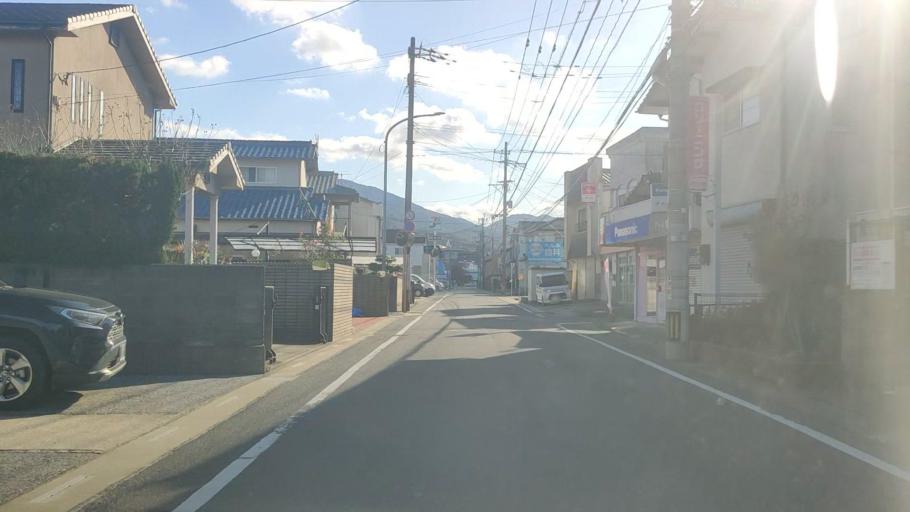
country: JP
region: Fukuoka
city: Fukuoka-shi
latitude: 33.5508
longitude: 130.3575
